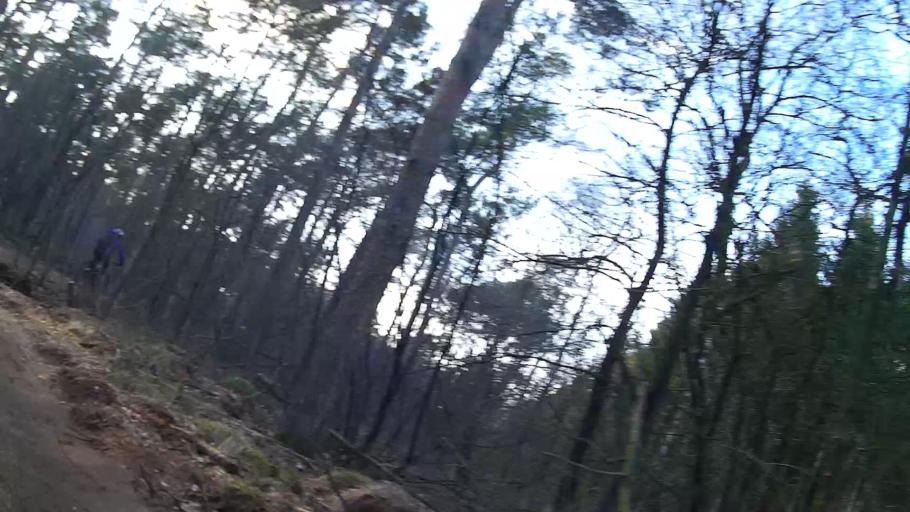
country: NL
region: Utrecht
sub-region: Gemeente Utrechtse Heuvelrug
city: Leersum
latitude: 52.0277
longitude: 5.4301
